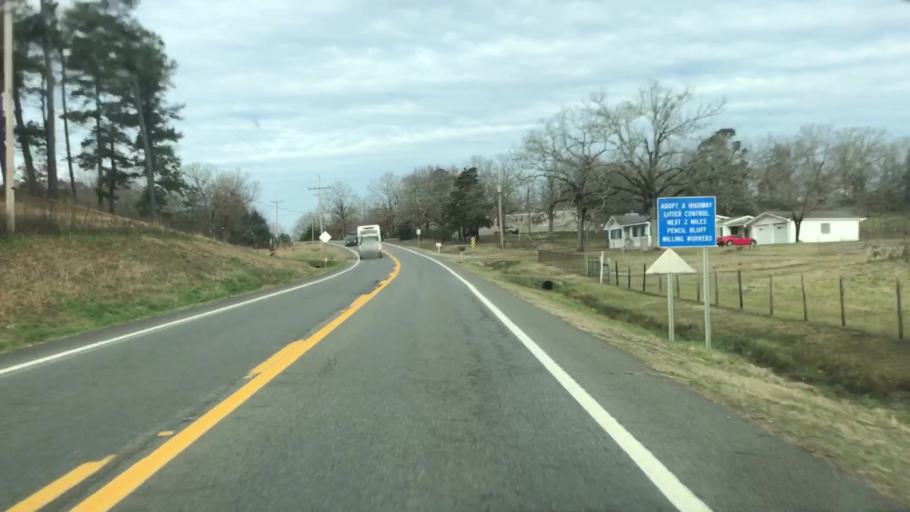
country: US
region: Arkansas
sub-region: Montgomery County
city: Mount Ida
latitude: 34.6232
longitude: -93.7261
